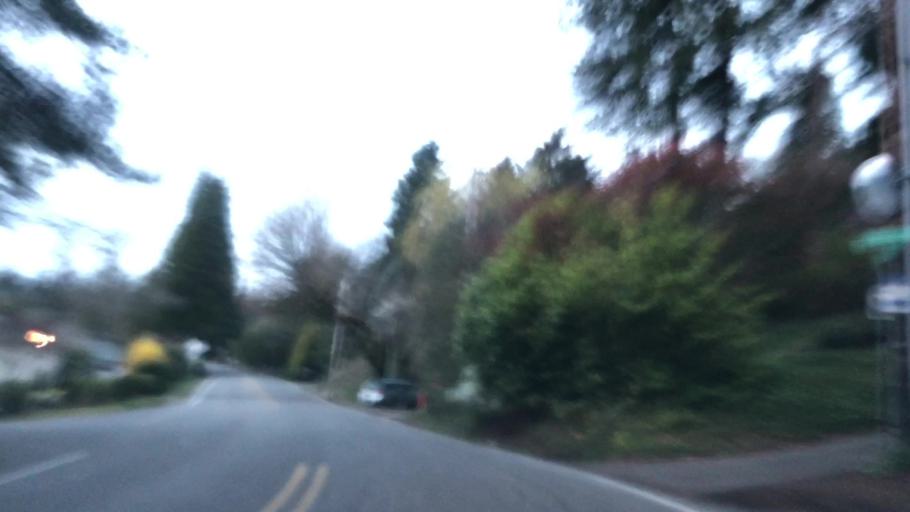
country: US
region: Oregon
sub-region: Multnomah County
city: Portland
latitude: 45.4961
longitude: -122.7116
